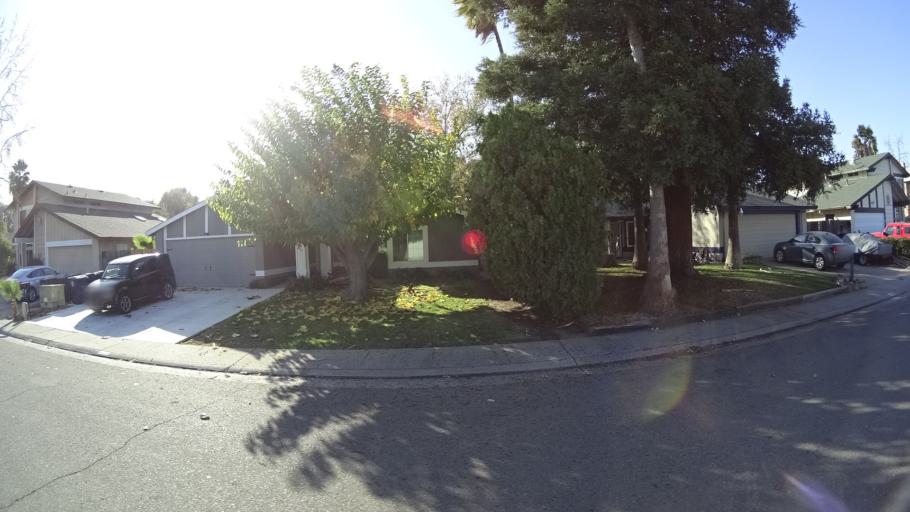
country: US
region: California
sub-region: Sacramento County
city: Antelope
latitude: 38.6983
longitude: -121.3136
